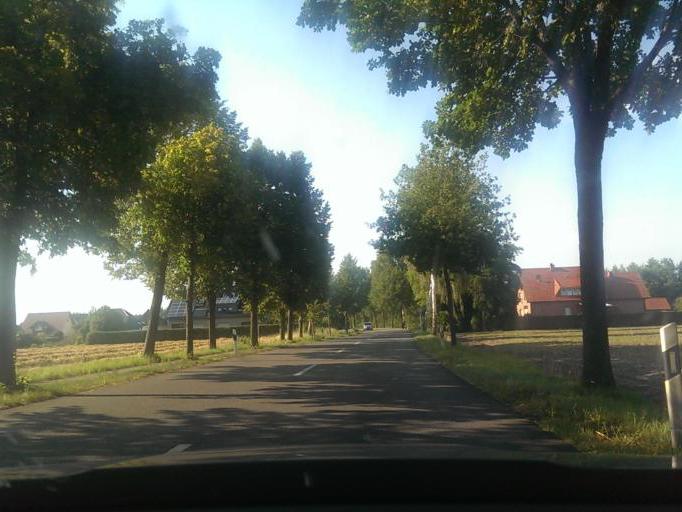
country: DE
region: North Rhine-Westphalia
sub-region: Regierungsbezirk Detmold
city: Delbruck
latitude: 51.7546
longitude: 8.5747
